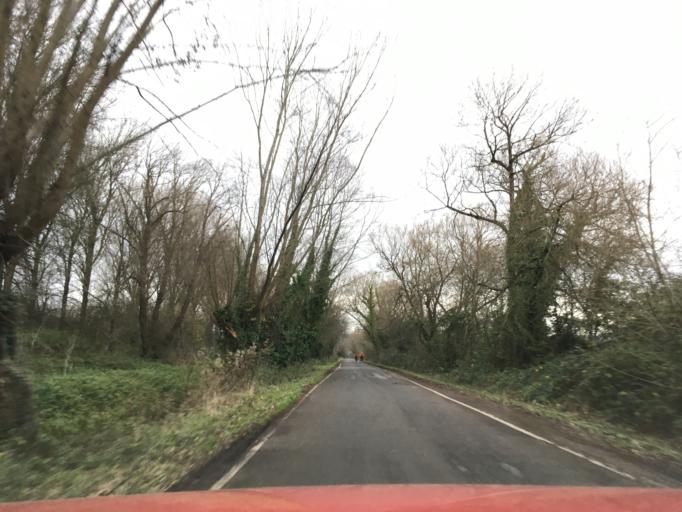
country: GB
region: Wales
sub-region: Newport
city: Bishton
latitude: 51.5750
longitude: -2.8694
